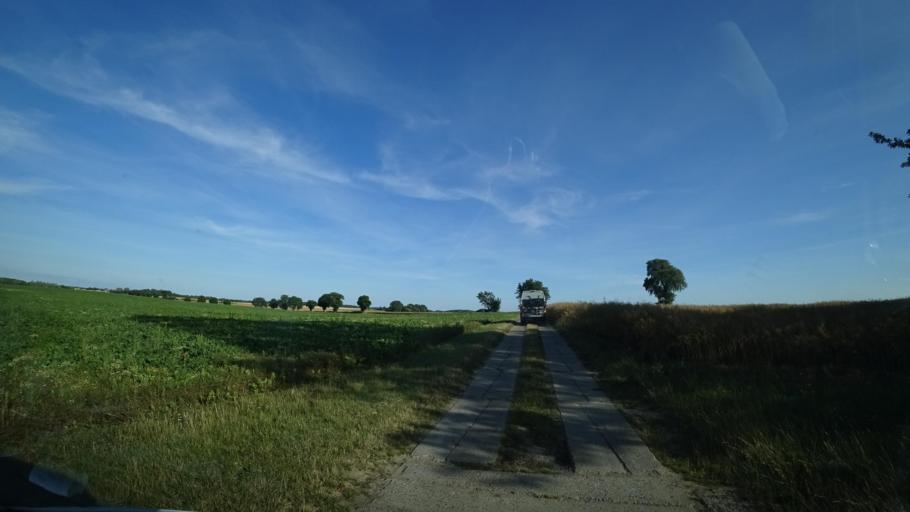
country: DE
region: Mecklenburg-Vorpommern
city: Rambin
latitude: 54.3238
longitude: 13.1757
